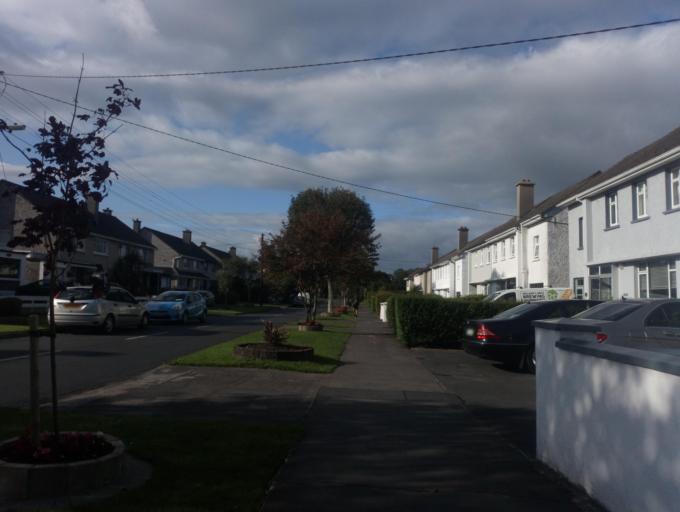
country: IE
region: Connaught
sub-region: County Galway
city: Gaillimh
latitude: 53.2636
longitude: -9.0770
